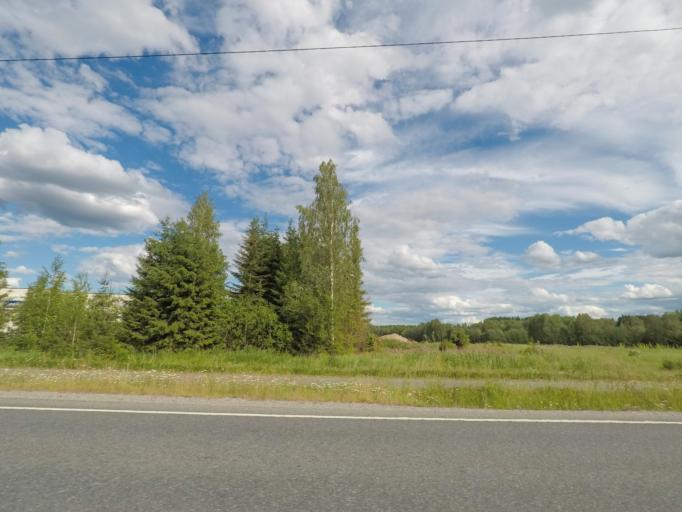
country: FI
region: Paijanne Tavastia
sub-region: Lahti
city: Lahti
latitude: 60.9558
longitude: 25.6179
